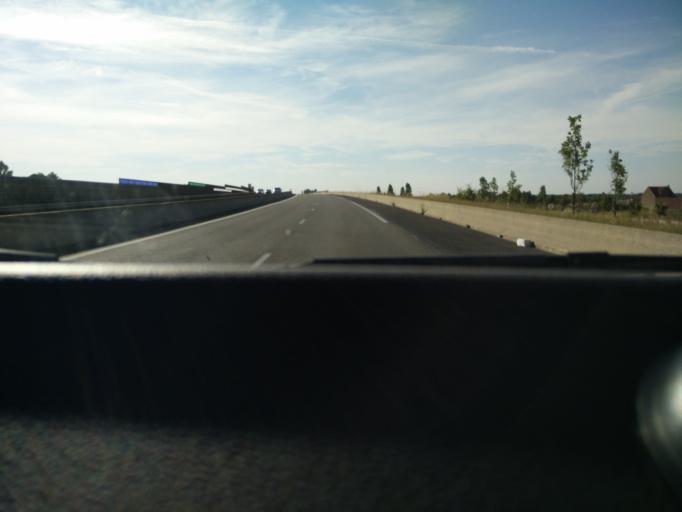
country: FR
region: Nord-Pas-de-Calais
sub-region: Departement du Nord
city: Abscon
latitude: 50.3427
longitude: 3.3128
